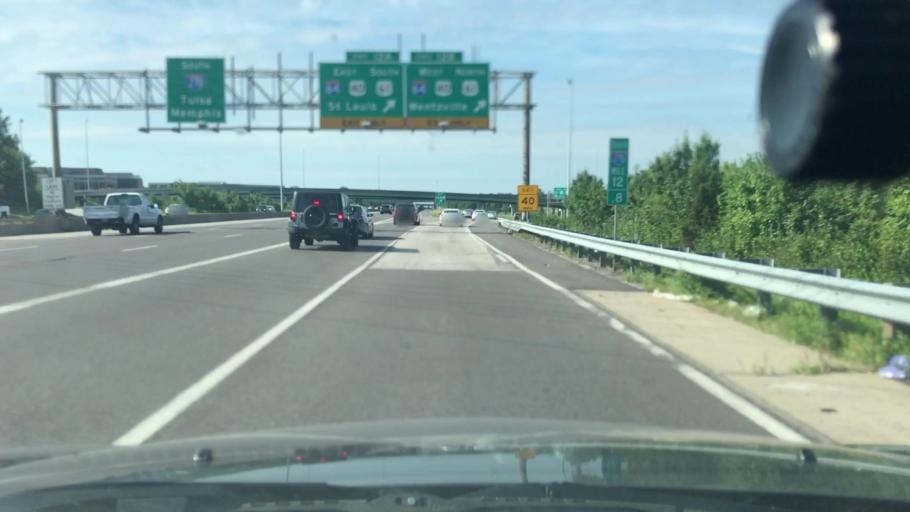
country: US
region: Missouri
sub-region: Saint Louis County
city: Creve Coeur
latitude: 38.6432
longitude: -90.4494
